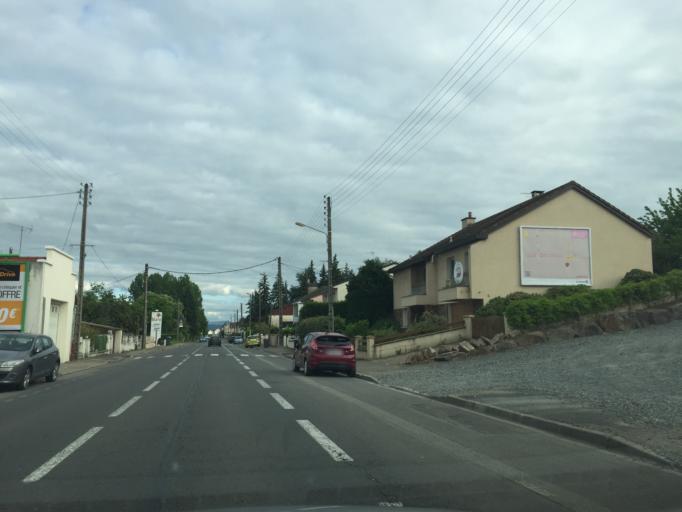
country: FR
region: Auvergne
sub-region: Departement de l'Allier
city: Bellerive-sur-Allier
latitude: 46.1243
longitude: 3.4023
